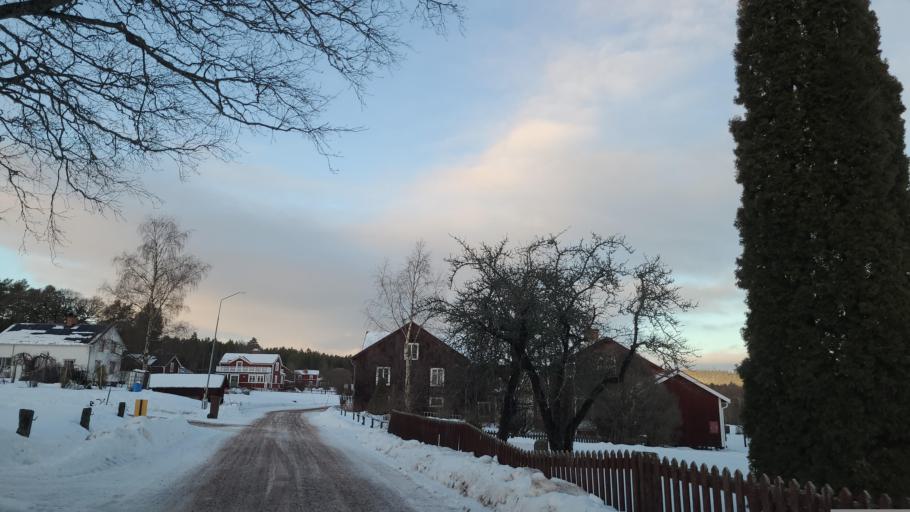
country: SE
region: Gaevleborg
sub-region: Bollnas Kommun
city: Kilafors
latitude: 61.3961
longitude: 16.6098
